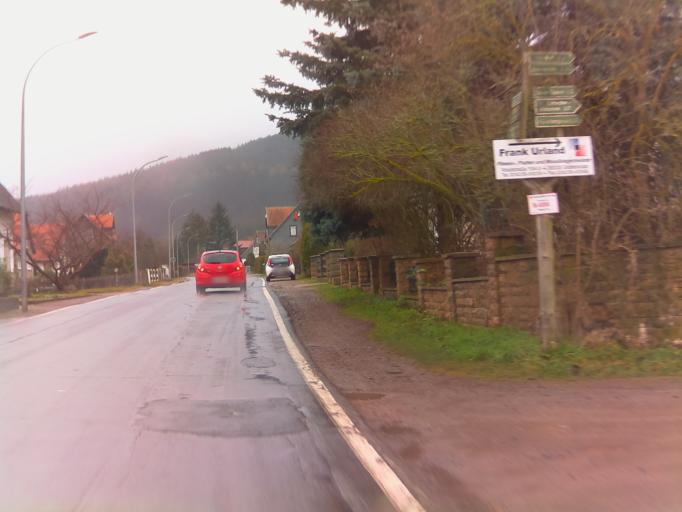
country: DE
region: Thuringia
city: Grafenroda
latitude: 50.7392
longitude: 10.7983
